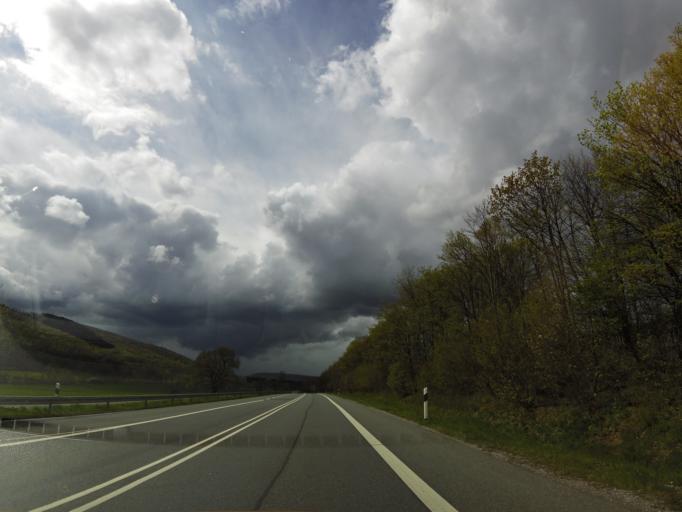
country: DE
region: Lower Saxony
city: Langelsheim
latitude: 51.9482
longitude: 10.3027
